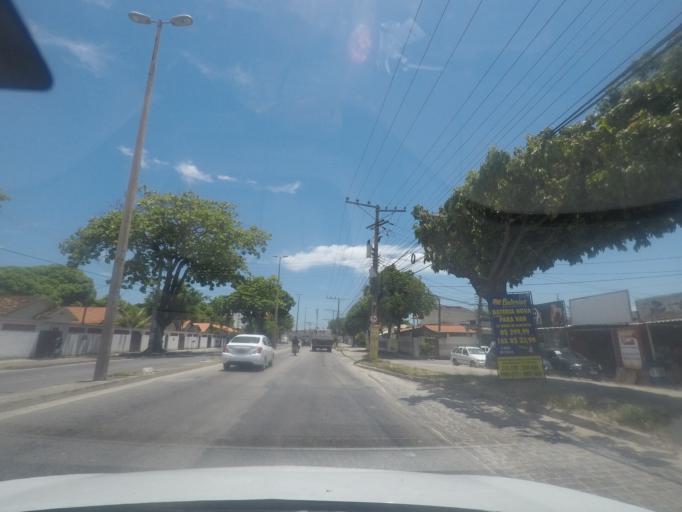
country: BR
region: Rio de Janeiro
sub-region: Itaguai
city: Itaguai
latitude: -22.9090
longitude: -43.6865
